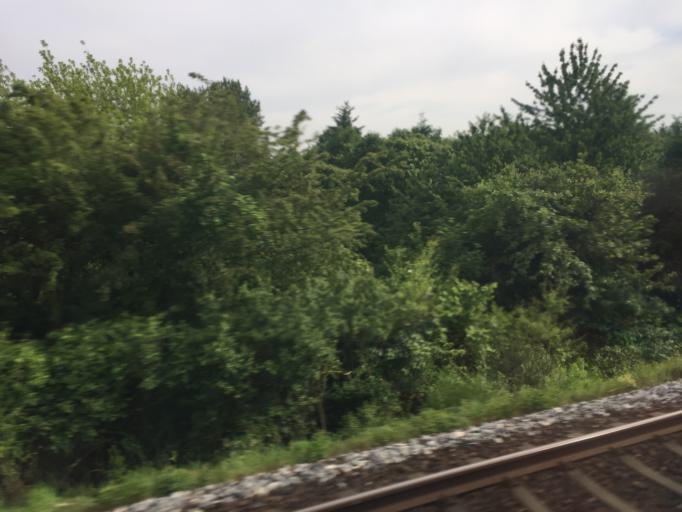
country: DK
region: South Denmark
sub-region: Odense Kommune
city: Odense
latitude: 55.3856
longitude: 10.3419
